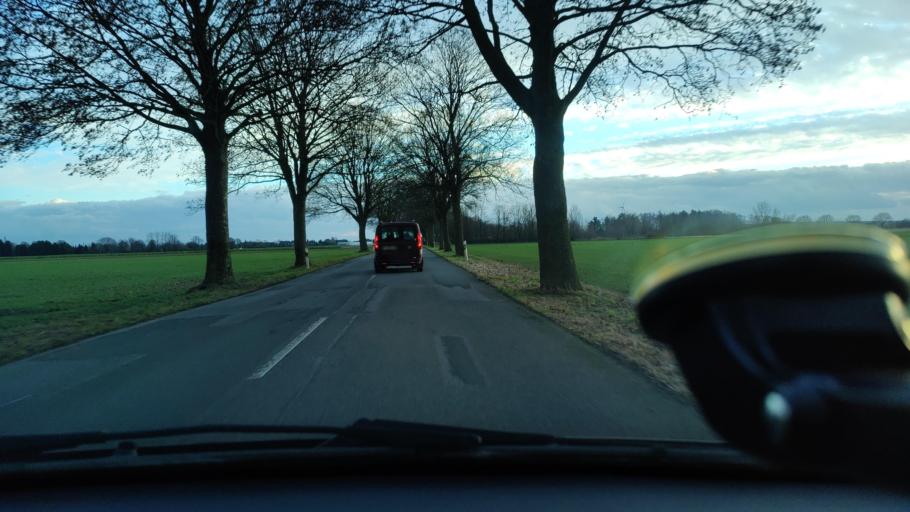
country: DE
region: North Rhine-Westphalia
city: Rees
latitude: 51.7373
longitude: 6.3995
